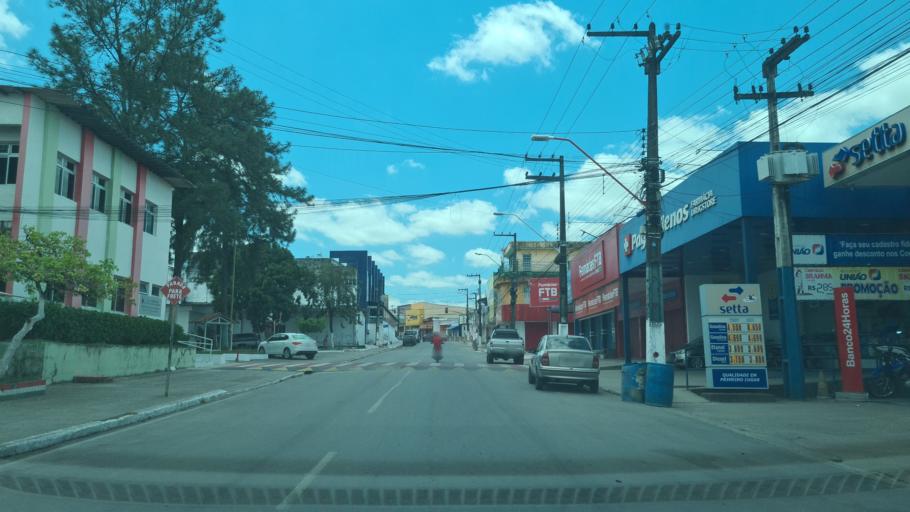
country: BR
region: Alagoas
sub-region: Uniao Dos Palmares
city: Uniao dos Palmares
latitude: -9.1586
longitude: -36.0321
